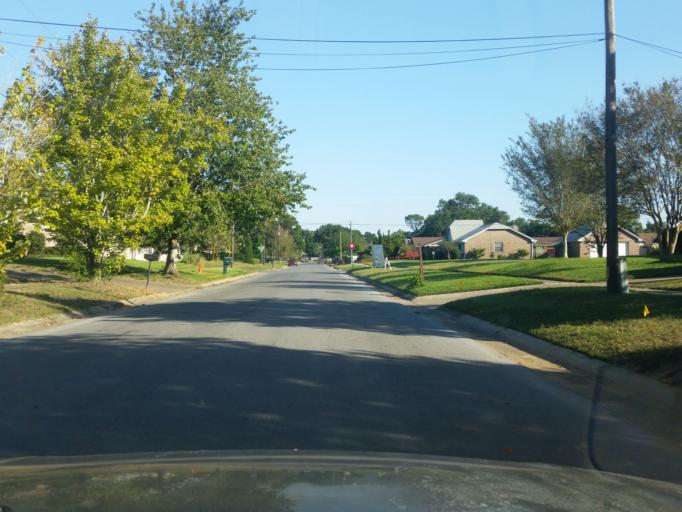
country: US
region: Florida
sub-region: Escambia County
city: Ferry Pass
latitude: 30.4930
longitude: -87.1708
